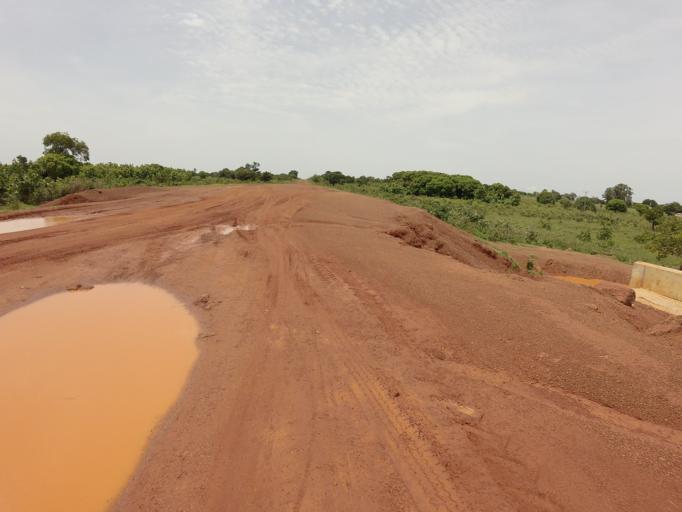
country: GH
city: Kpandae
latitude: 8.7624
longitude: 0.0584
